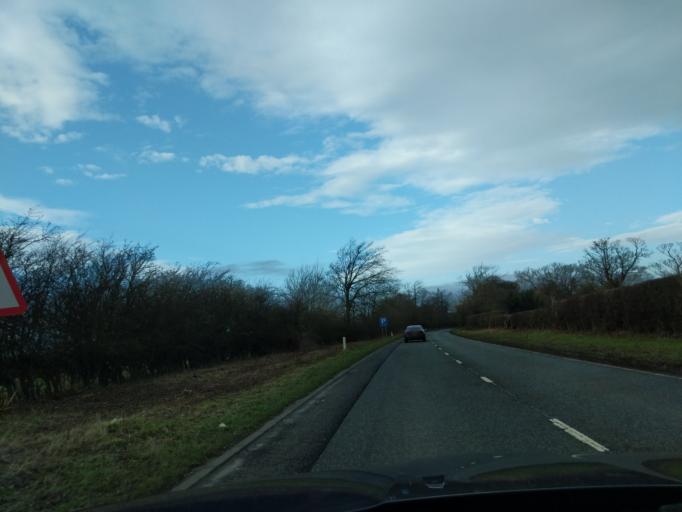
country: GB
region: England
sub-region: Northumberland
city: Darras Hall
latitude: 55.0693
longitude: -1.7897
